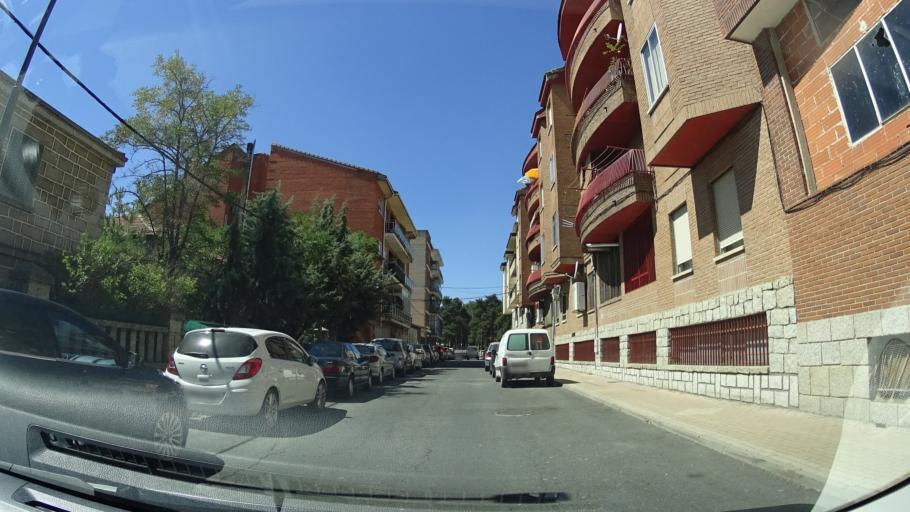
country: ES
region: Castille and Leon
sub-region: Provincia de Avila
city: Las Navas del Marques
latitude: 40.5991
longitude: -4.3362
